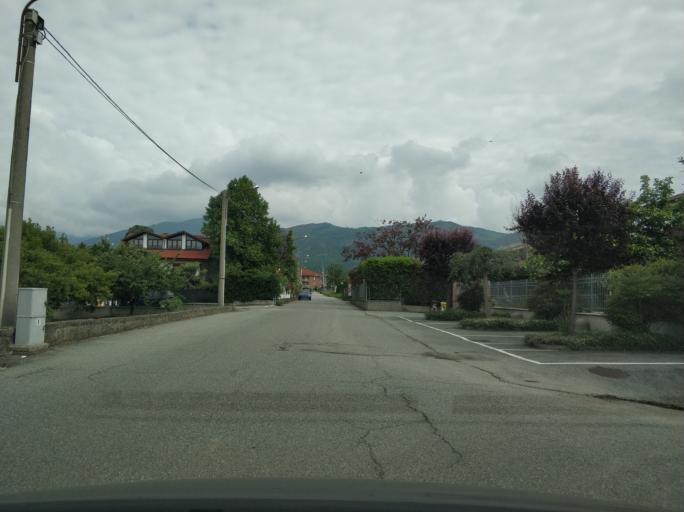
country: IT
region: Piedmont
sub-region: Provincia di Torino
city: Balangero
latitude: 45.2628
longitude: 7.5227
